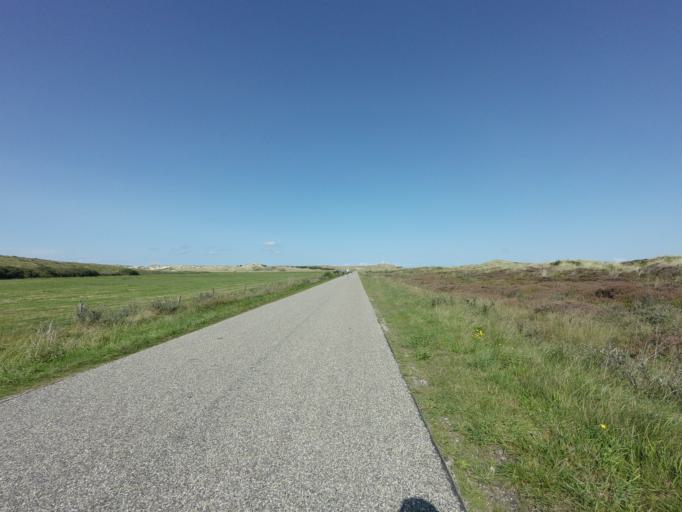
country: NL
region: Friesland
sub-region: Gemeente Terschelling
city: West-Terschelling
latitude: 53.4171
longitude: 5.3879
